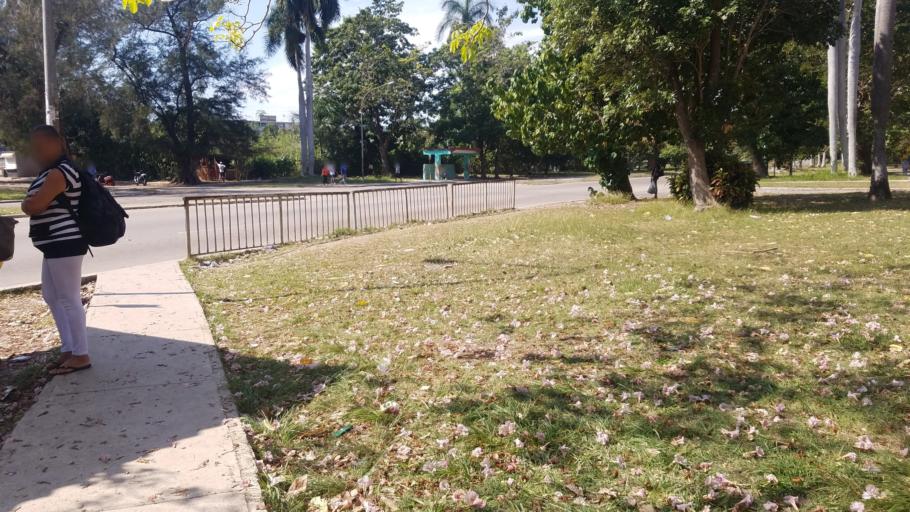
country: CU
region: La Habana
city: Habana del Este
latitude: 23.1512
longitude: -82.3065
